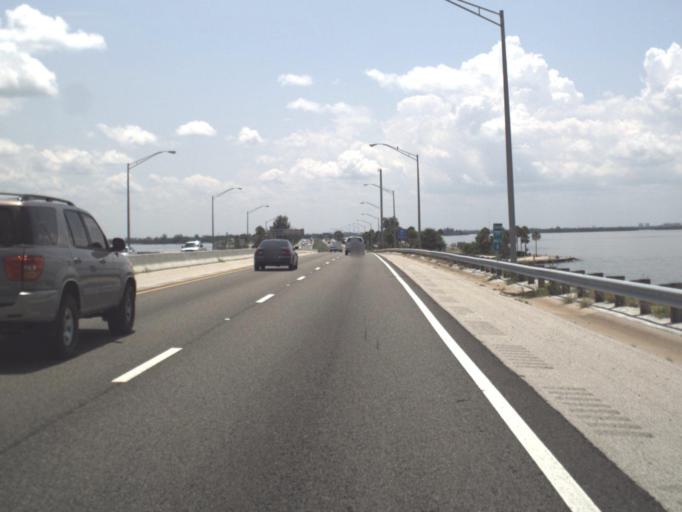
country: US
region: Florida
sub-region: Manatee County
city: Memphis
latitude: 27.5922
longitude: -82.6298
